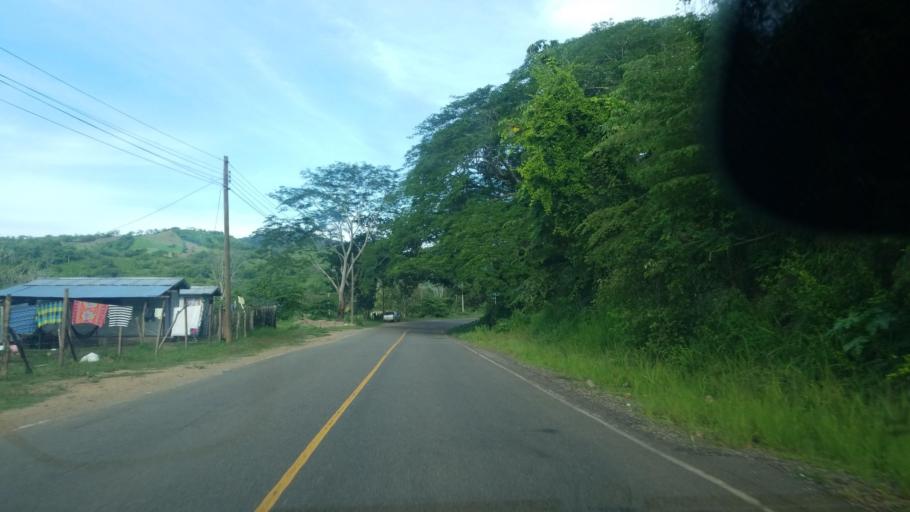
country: HN
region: Santa Barbara
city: Trinidad
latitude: 15.1215
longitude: -88.2029
